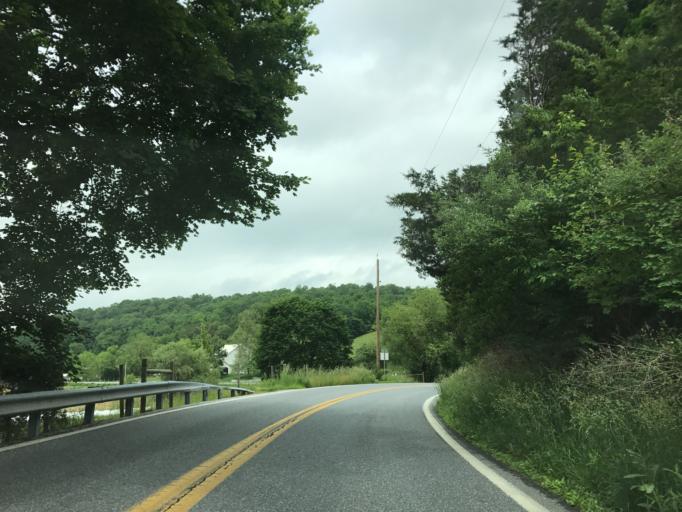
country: US
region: Pennsylvania
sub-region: York County
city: Dallastown
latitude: 39.8490
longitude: -76.6527
